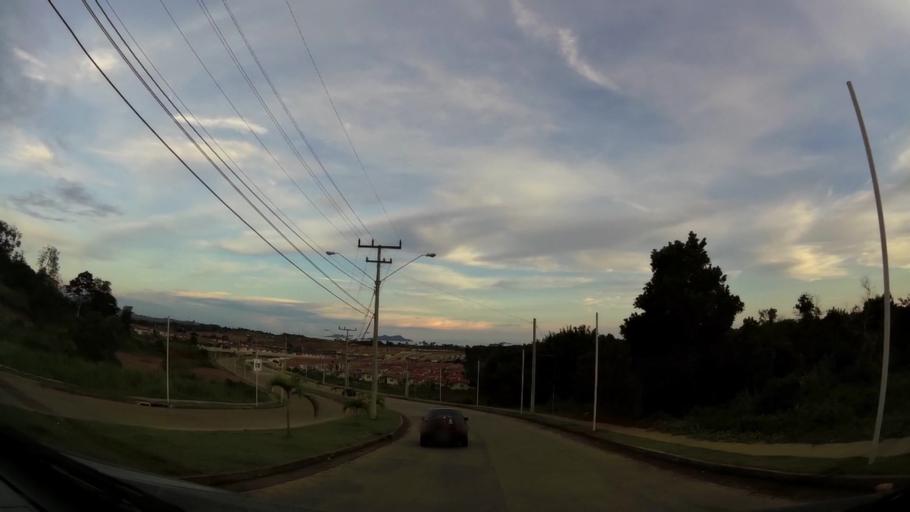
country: PA
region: Panama
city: La Chorrera
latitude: 8.8601
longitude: -79.7669
